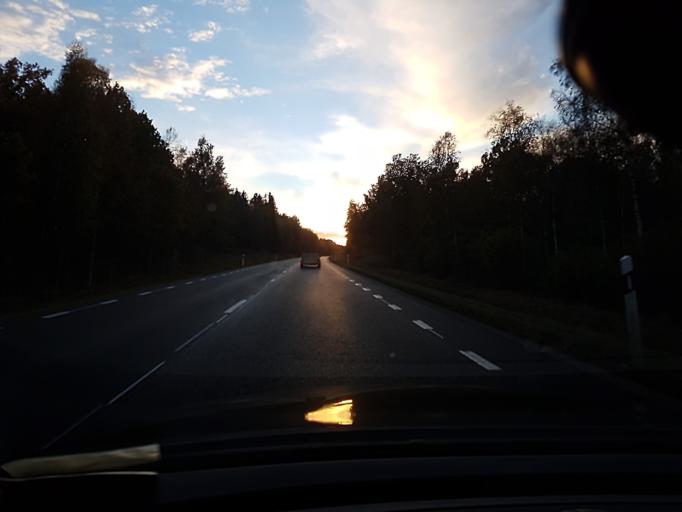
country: SE
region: Kronoberg
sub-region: Ljungby Kommun
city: Ljungby
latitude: 56.7578
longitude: 13.7616
